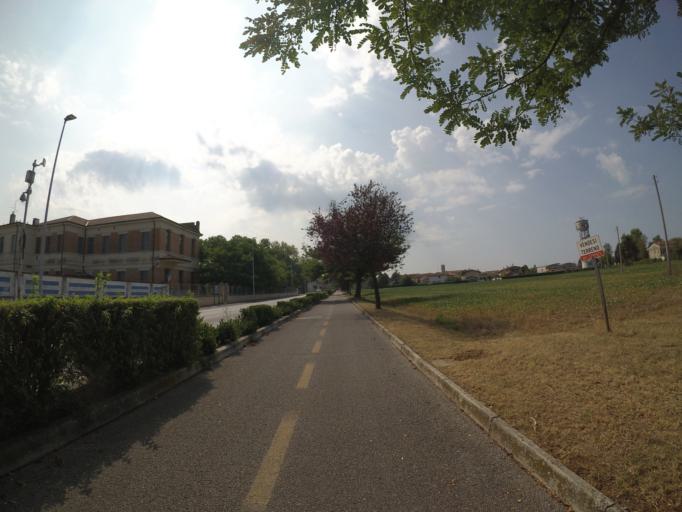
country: IT
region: Friuli Venezia Giulia
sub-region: Provincia di Udine
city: Precenicco
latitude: 45.7928
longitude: 13.0774
